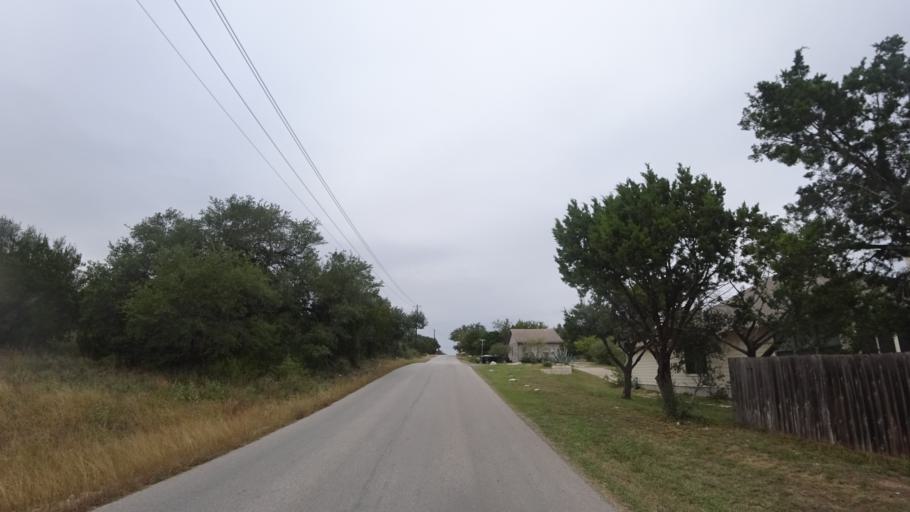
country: US
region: Texas
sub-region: Travis County
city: Hudson Bend
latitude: 30.3743
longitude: -97.9249
